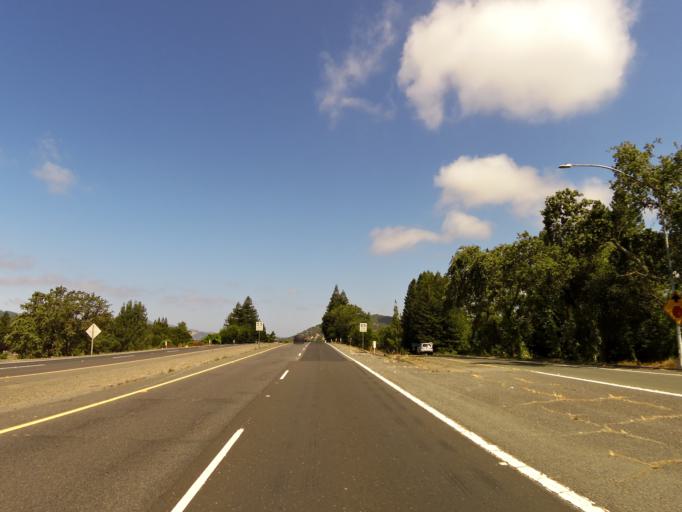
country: US
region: California
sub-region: Napa County
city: Yountville
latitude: 38.3962
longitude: -122.3574
